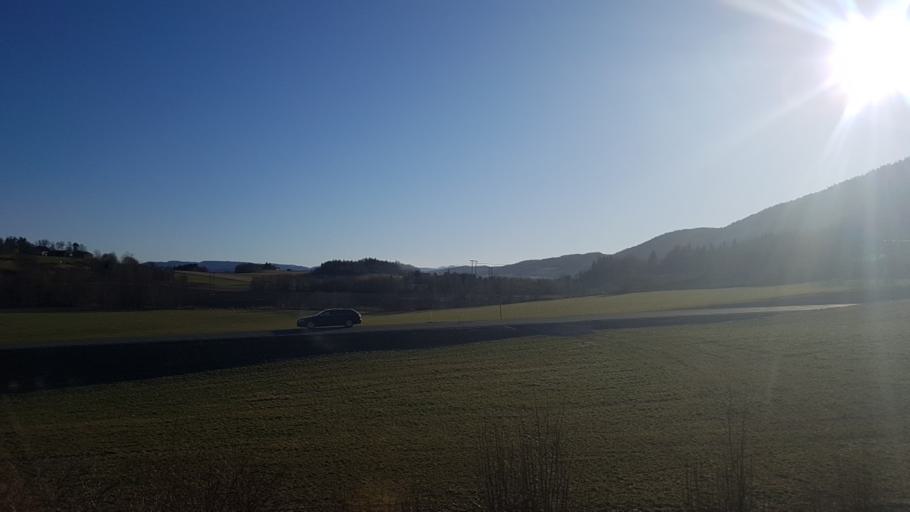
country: NO
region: Nord-Trondelag
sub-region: Stjordal
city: Stjordalshalsen
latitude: 63.6023
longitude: 11.0274
